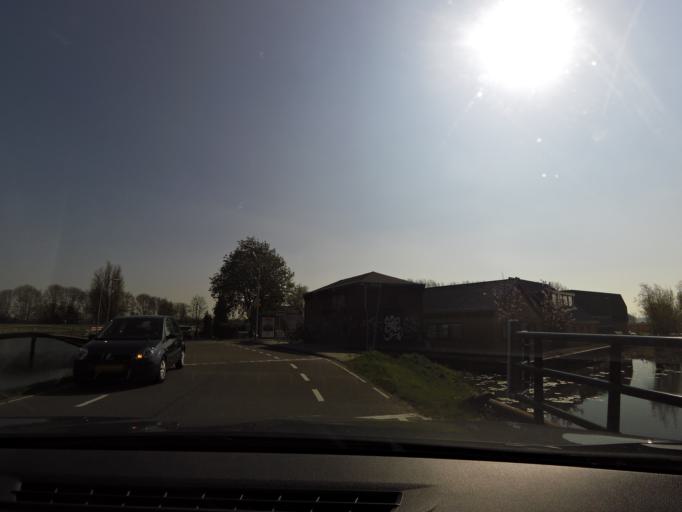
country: NL
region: South Holland
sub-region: Gemeente Westland
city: De Lier
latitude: 51.9512
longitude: 4.2780
